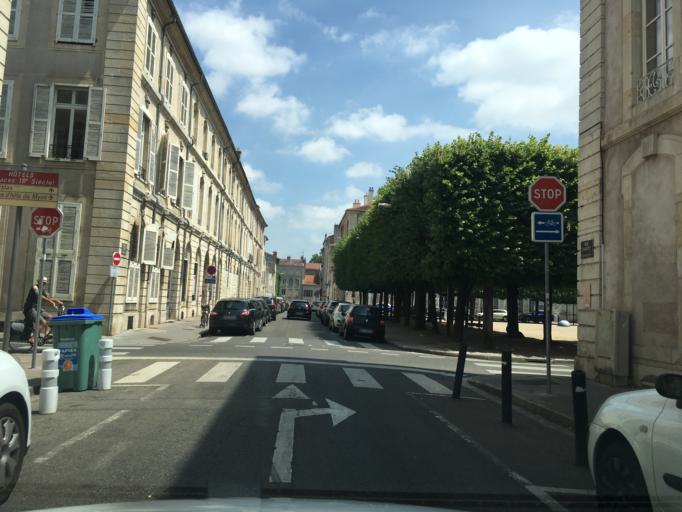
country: FR
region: Lorraine
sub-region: Departement de Meurthe-et-Moselle
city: Nancy
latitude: 48.6938
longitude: 6.1855
